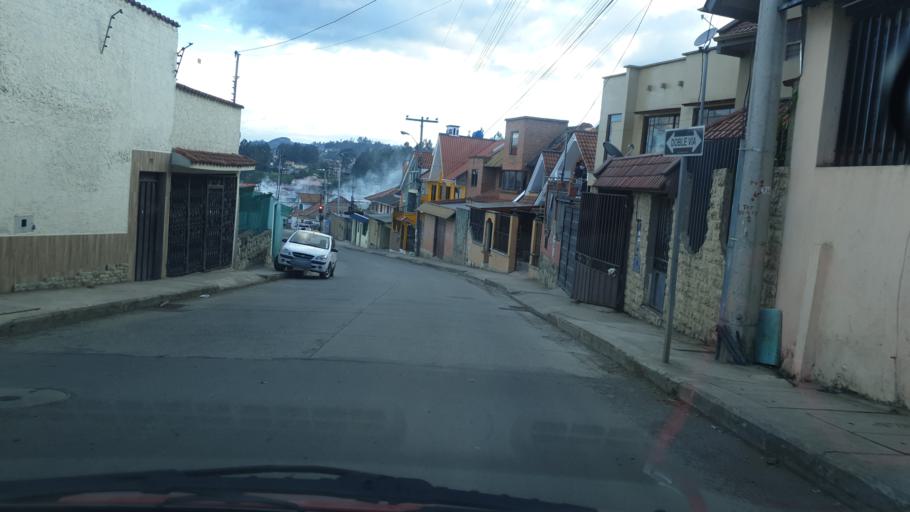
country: EC
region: Azuay
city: Cuenca
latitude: -2.8842
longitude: -79.0429
